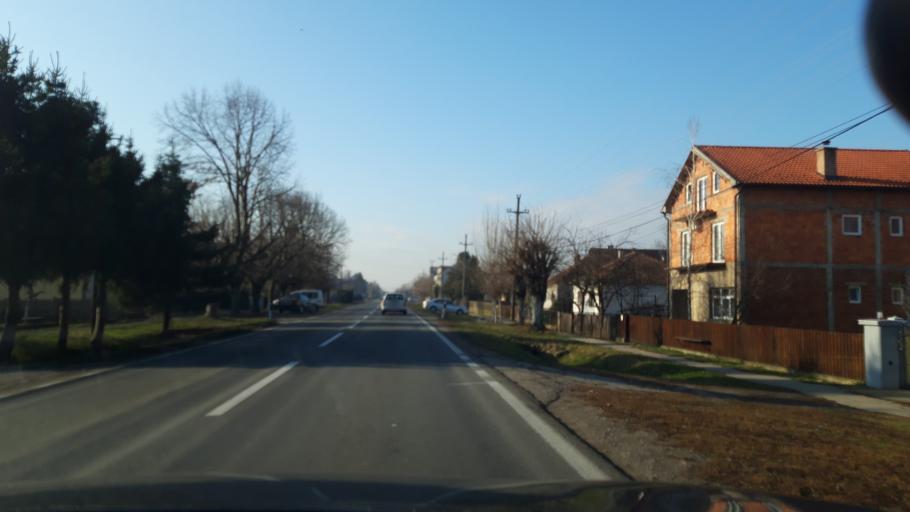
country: RS
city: Prnjavor
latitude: 44.7021
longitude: 19.3937
